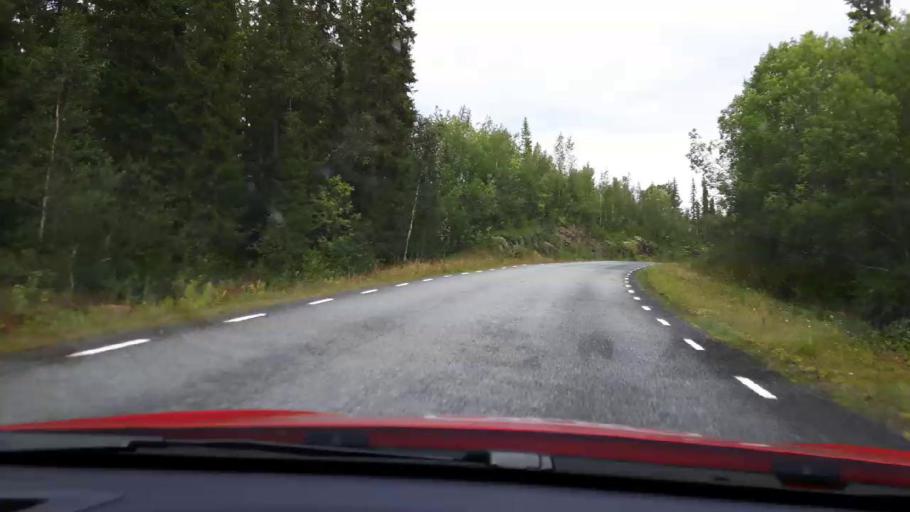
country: SE
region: Jaemtland
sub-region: Are Kommun
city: Are
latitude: 63.7072
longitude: 12.9490
